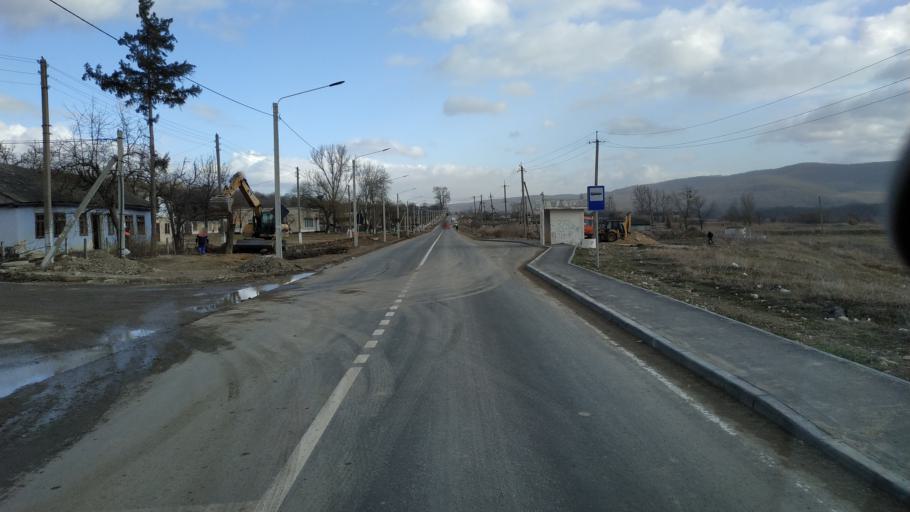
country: MD
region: Calarasi
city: Calarasi
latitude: 47.3214
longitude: 28.1081
